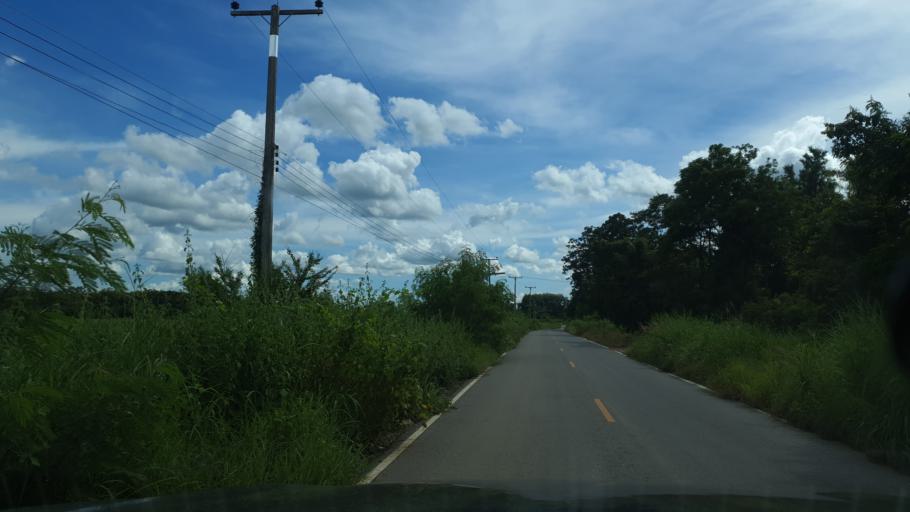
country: TH
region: Sukhothai
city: Thung Saliam
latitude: 17.3536
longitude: 99.6419
